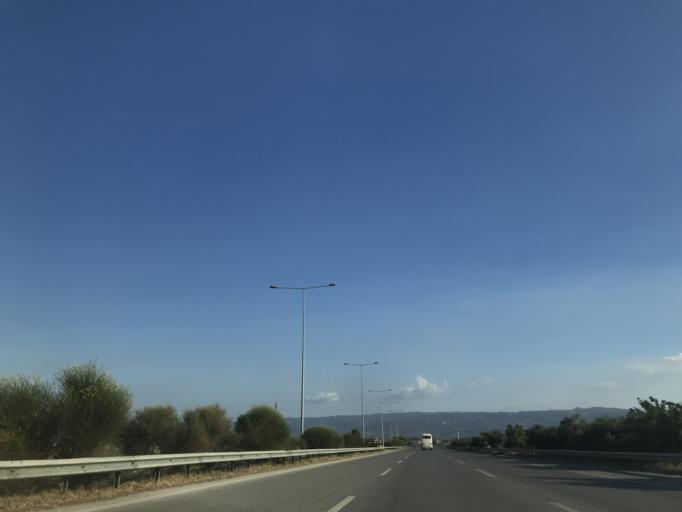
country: TR
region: Aydin
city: Aydin
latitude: 37.8360
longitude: 27.8098
